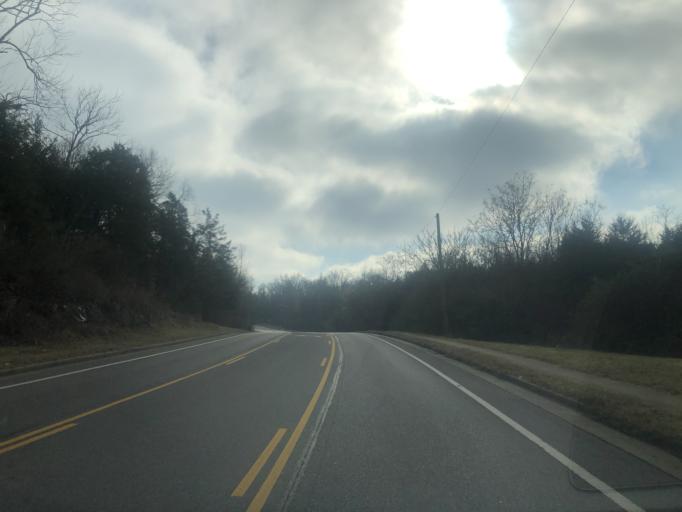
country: US
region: Tennessee
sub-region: Rutherford County
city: La Vergne
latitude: 36.0743
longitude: -86.6478
